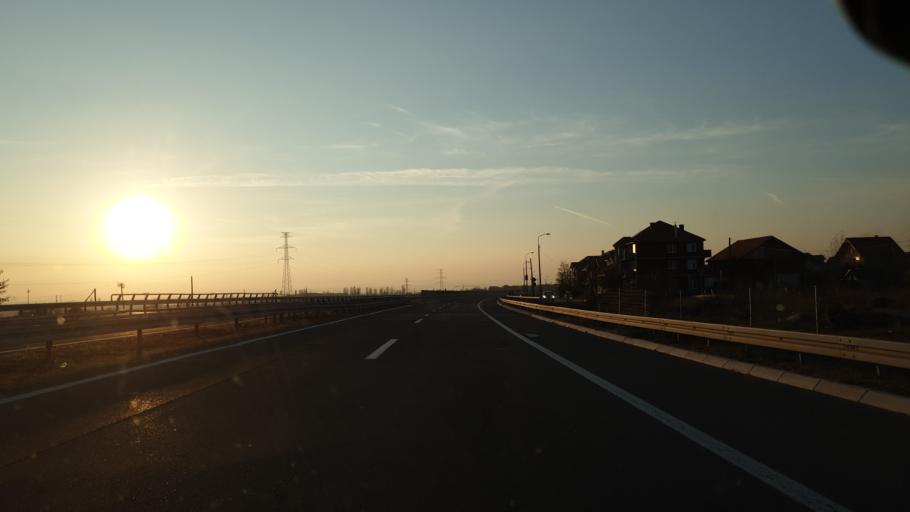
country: RS
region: Central Serbia
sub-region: Nisavski Okrug
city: Nis
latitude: 43.3423
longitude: 21.8925
